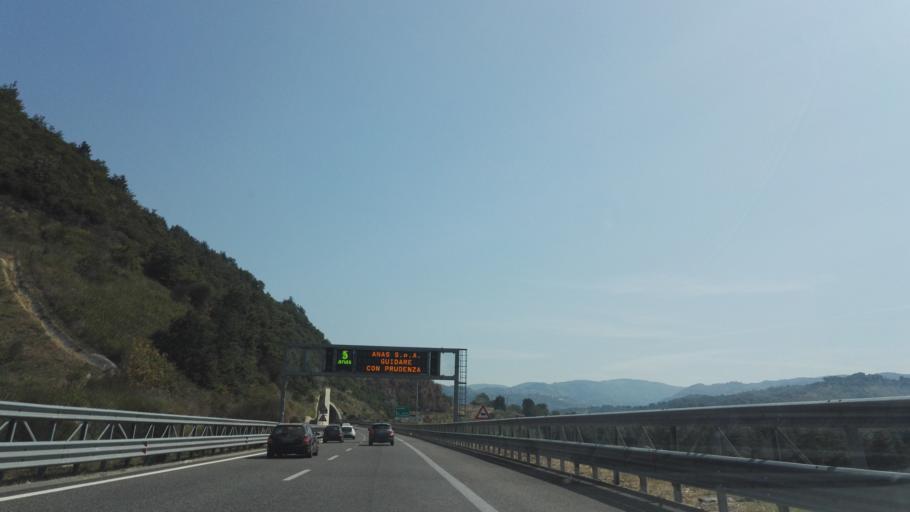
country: IT
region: Calabria
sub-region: Provincia di Catanzaro
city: Martirano
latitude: 39.0966
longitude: 16.2368
